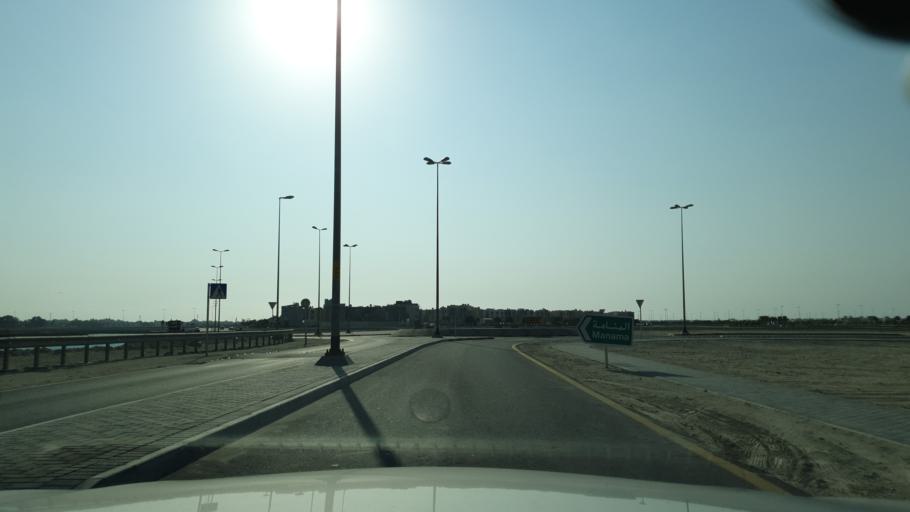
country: BH
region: Manama
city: Jidd Hafs
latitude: 26.2310
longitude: 50.4603
